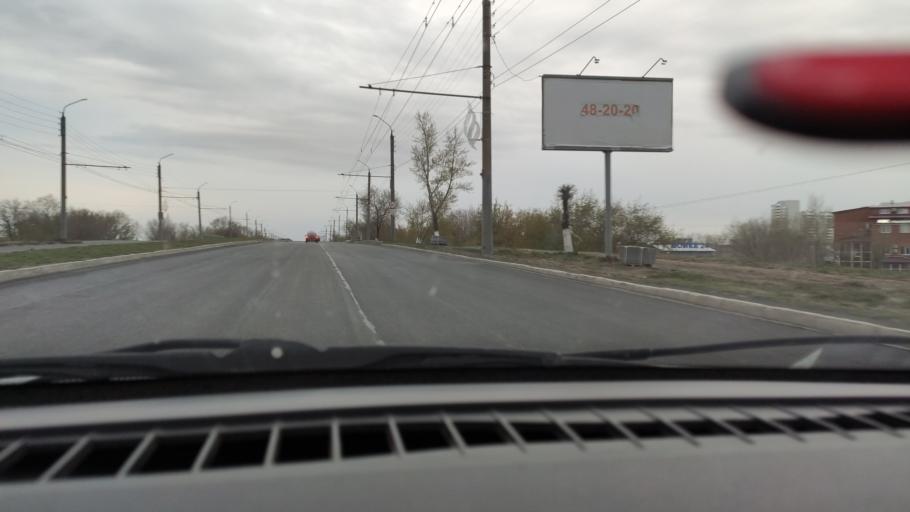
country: RU
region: Orenburg
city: Orenburg
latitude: 51.8033
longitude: 55.1068
